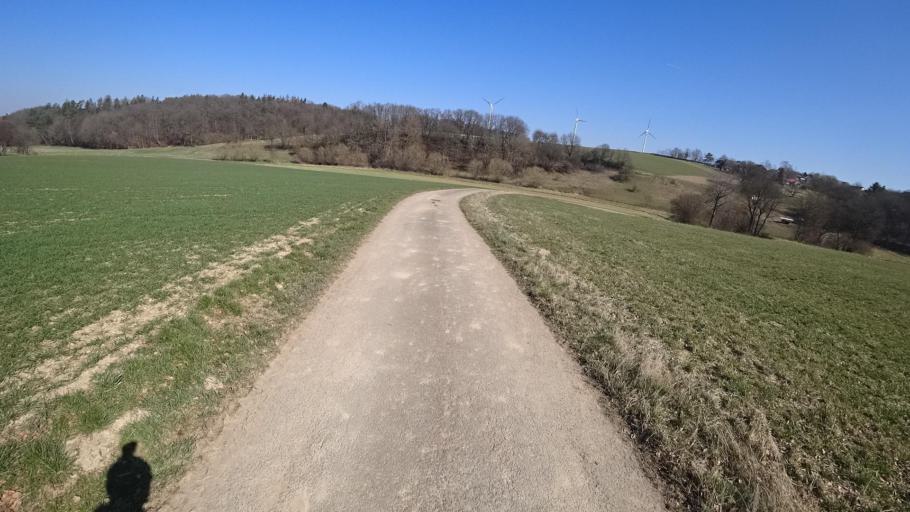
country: DE
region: Rheinland-Pfalz
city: Wahlbach
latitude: 50.0012
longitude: 7.5868
